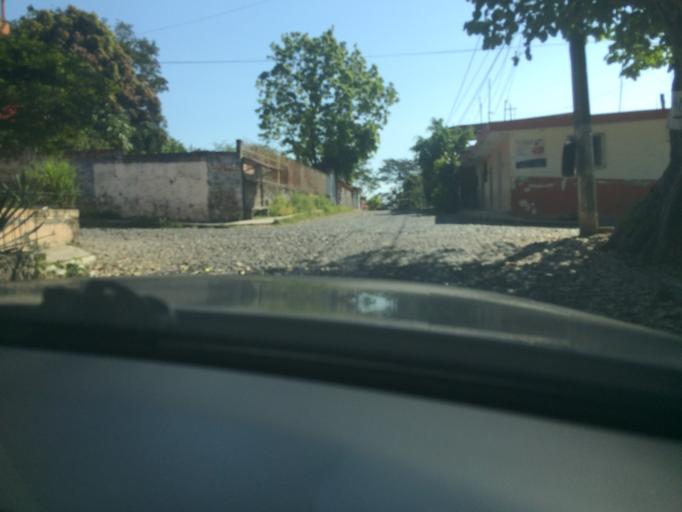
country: MX
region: Colima
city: Suchitlan
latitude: 19.3741
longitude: -103.7142
